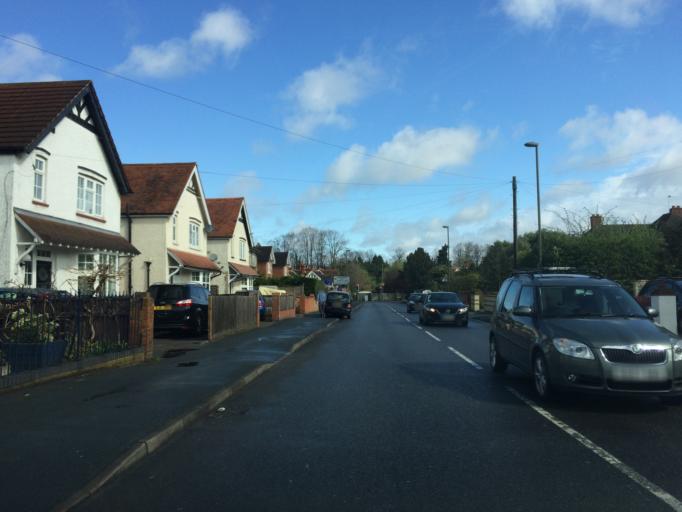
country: GB
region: England
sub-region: Surrey
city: Chertsey
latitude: 51.3891
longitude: -0.4946
